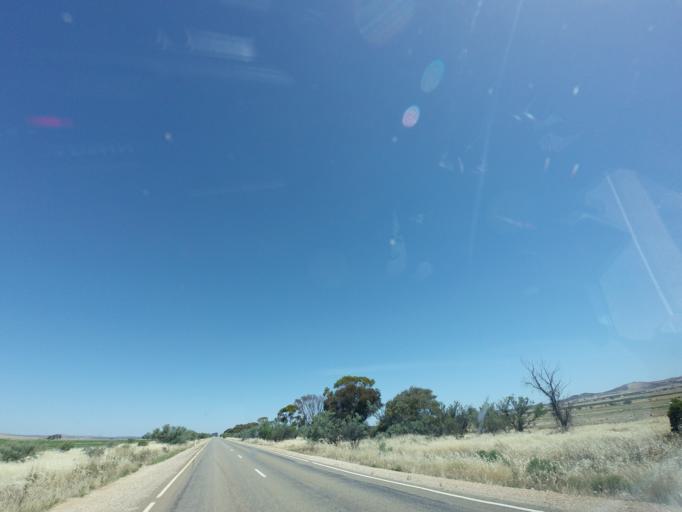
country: AU
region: South Australia
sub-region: Peterborough
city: Peterborough
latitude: -32.7906
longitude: 138.6741
